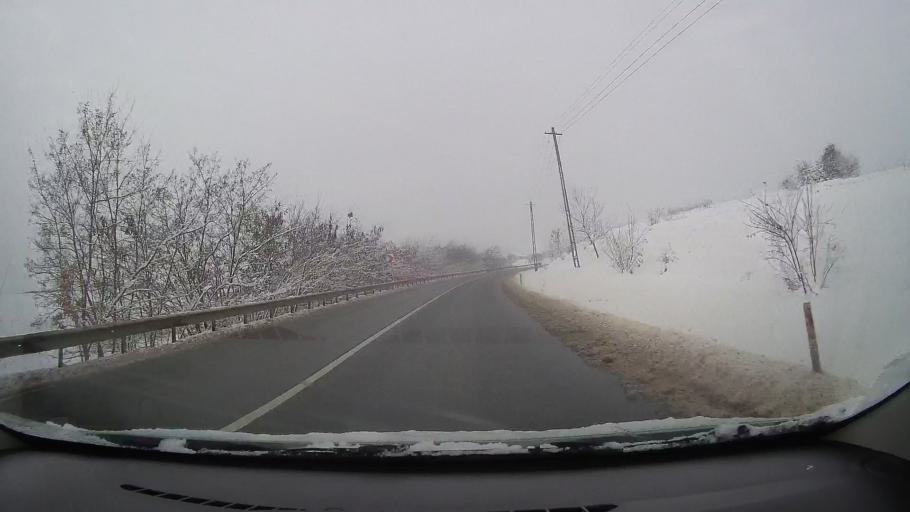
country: RO
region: Alba
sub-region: Municipiul Sebes
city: Lancram
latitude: 45.9843
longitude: 23.5126
